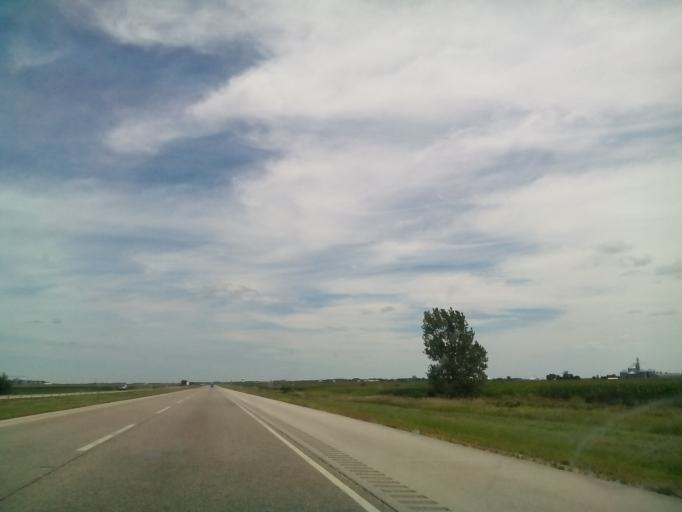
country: US
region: Illinois
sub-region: DeKalb County
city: Malta
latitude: 41.8999
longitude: -88.8385
